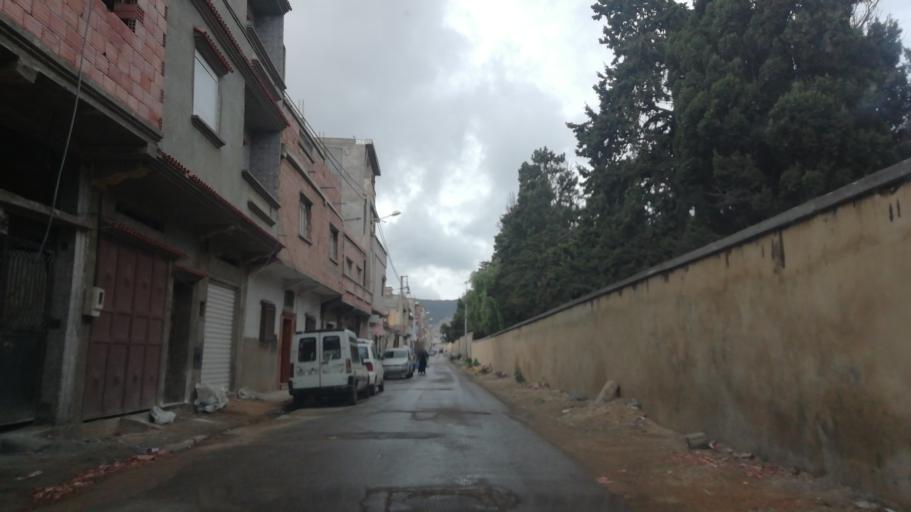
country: DZ
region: Oran
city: Oran
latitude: 35.6898
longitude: -0.6363
